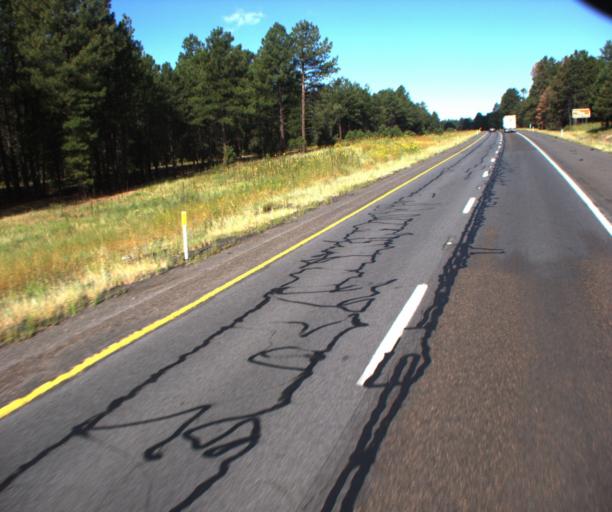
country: US
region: Arizona
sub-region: Coconino County
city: Parks
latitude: 35.2491
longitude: -111.8549
